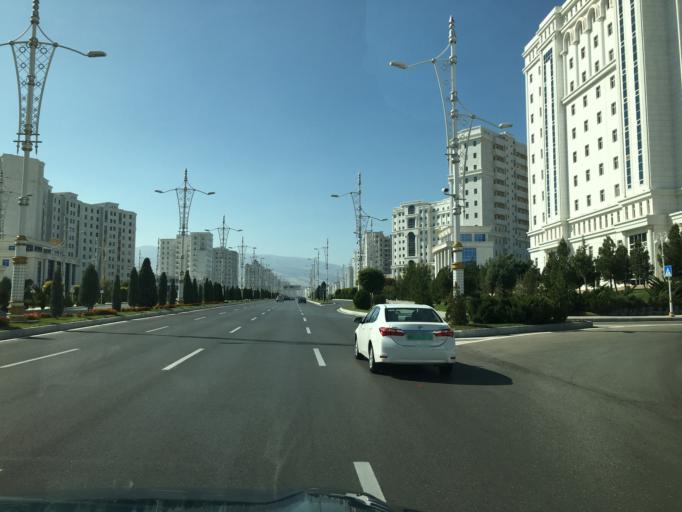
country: TM
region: Ahal
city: Ashgabat
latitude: 37.9238
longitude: 58.3654
